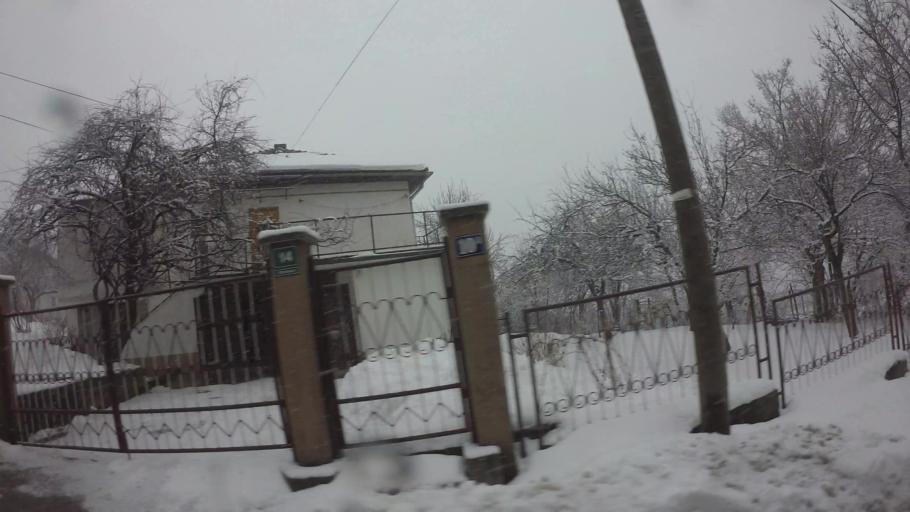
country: BA
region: Federation of Bosnia and Herzegovina
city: Kobilja Glava
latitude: 43.8525
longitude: 18.4443
